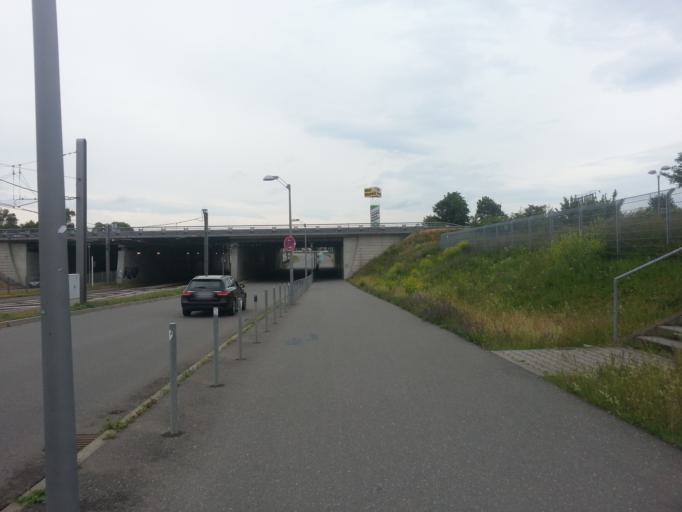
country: DE
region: Rheinland-Pfalz
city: Altrip
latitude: 49.4658
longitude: 8.5213
